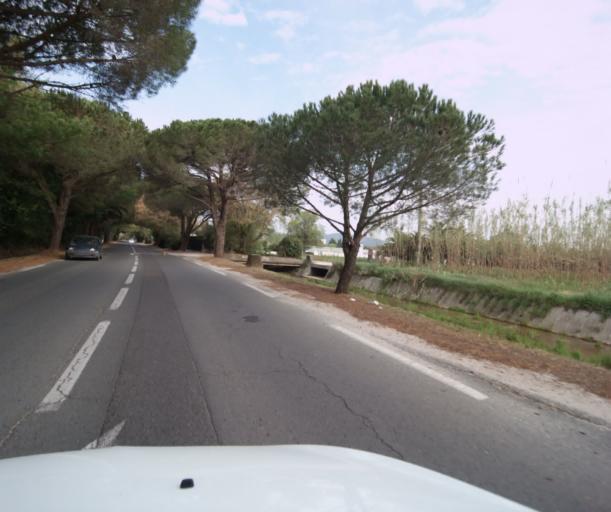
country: FR
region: Provence-Alpes-Cote d'Azur
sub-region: Departement du Var
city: Hyeres
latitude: 43.1116
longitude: 6.1662
